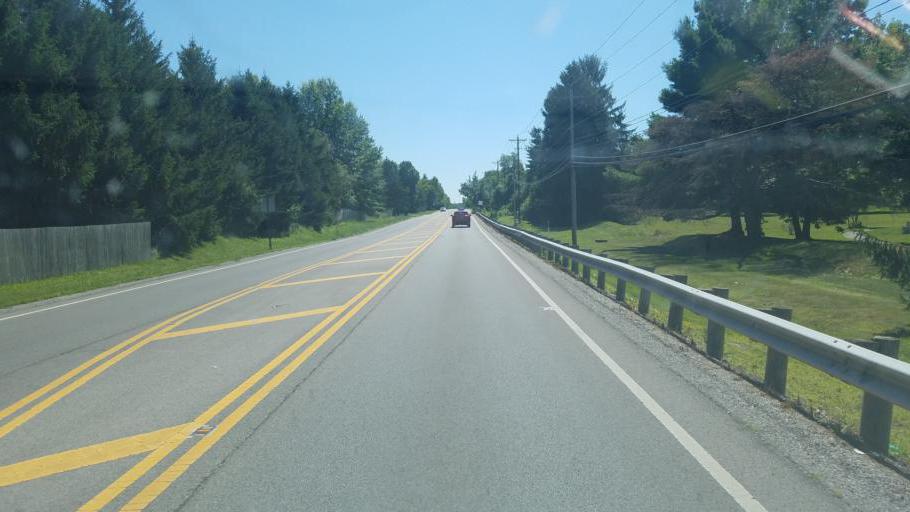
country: US
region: Ohio
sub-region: Franklin County
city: Huber Ridge
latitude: 40.0665
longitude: -82.9116
